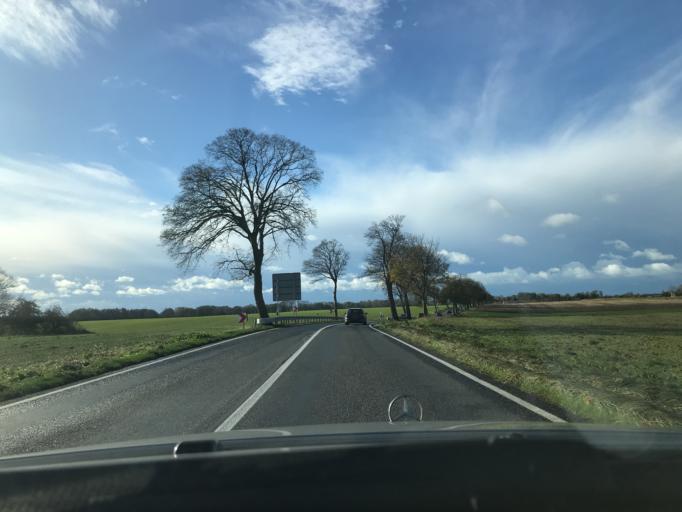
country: DE
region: Mecklenburg-Vorpommern
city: Zussow
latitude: 53.9570
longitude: 13.5121
